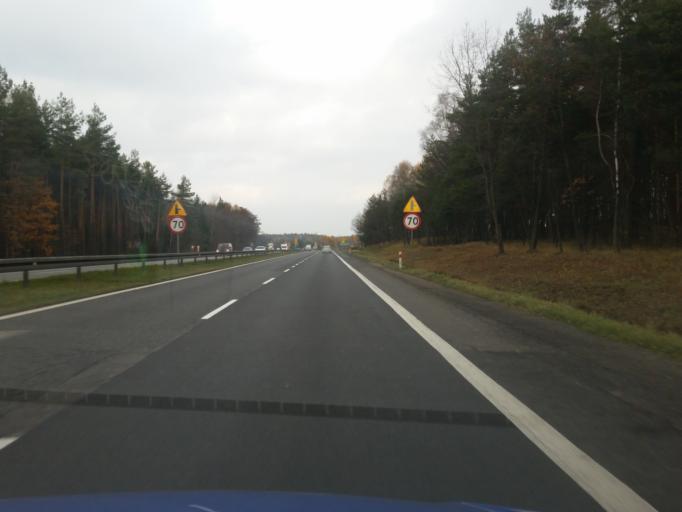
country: PL
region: Silesian Voivodeship
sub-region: Powiat bedzinski
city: Siewierz
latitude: 50.5303
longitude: 19.1911
